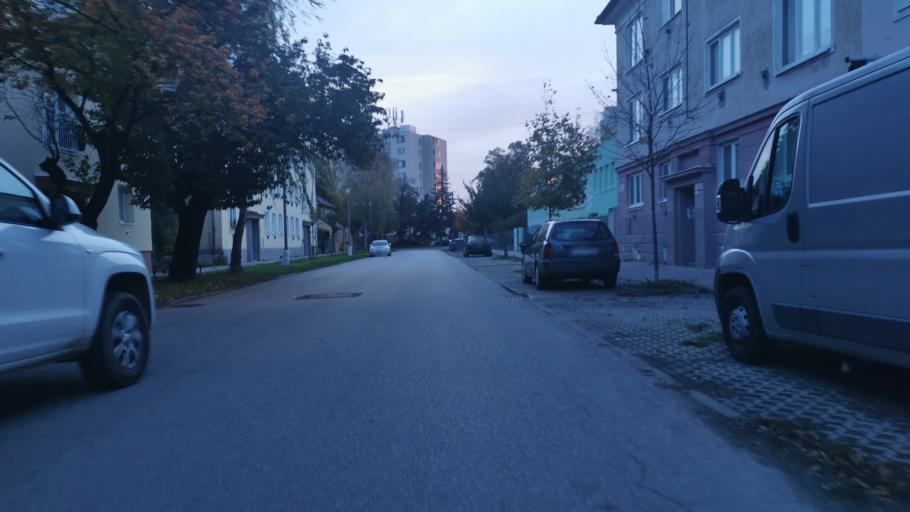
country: SK
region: Trnavsky
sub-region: Okres Skalica
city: Skalica
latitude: 48.8420
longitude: 17.2302
